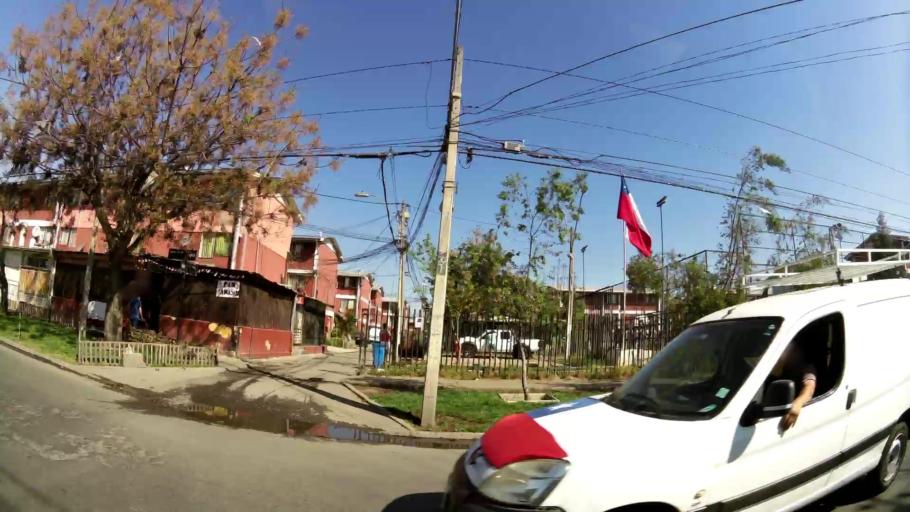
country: CL
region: Santiago Metropolitan
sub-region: Provincia de Santiago
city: La Pintana
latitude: -33.5393
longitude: -70.6012
